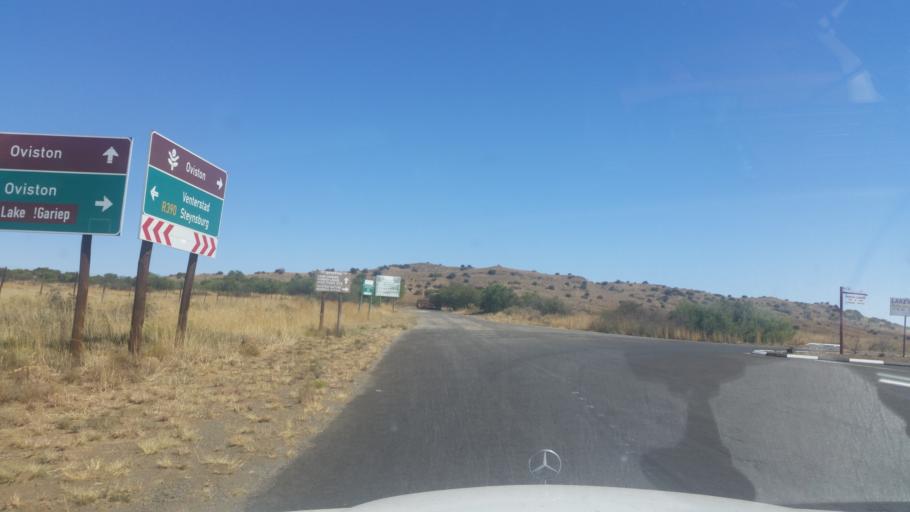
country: ZA
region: Eastern Cape
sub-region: Joe Gqabi District Municipality
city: Burgersdorp
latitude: -30.7440
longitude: 25.7567
